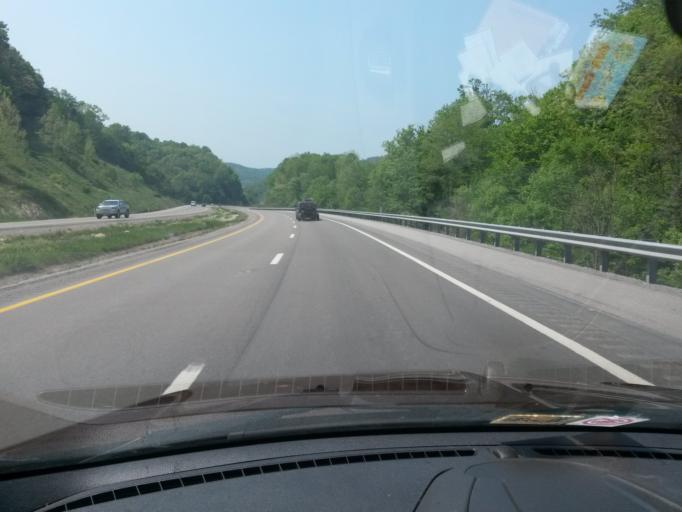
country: US
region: West Virginia
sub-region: Lewis County
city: Weston
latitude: 38.8943
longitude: -80.6250
